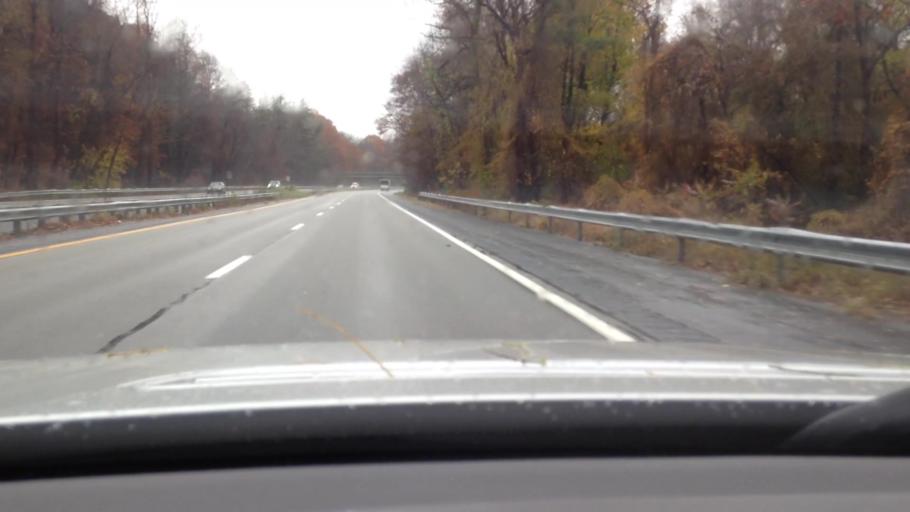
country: US
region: New York
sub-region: Westchester County
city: Crugers
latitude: 41.2393
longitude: -73.9153
